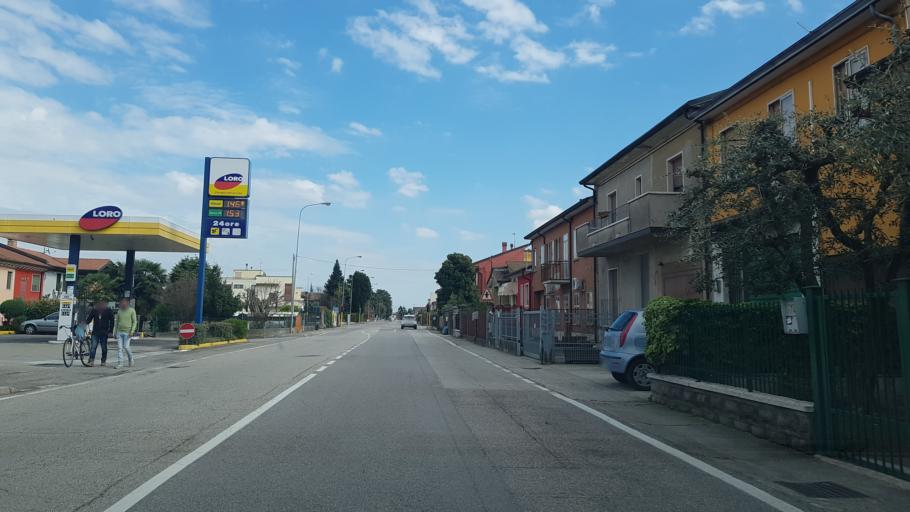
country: IT
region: Veneto
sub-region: Provincia di Verona
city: Belfiore
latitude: 45.3818
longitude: 11.2111
